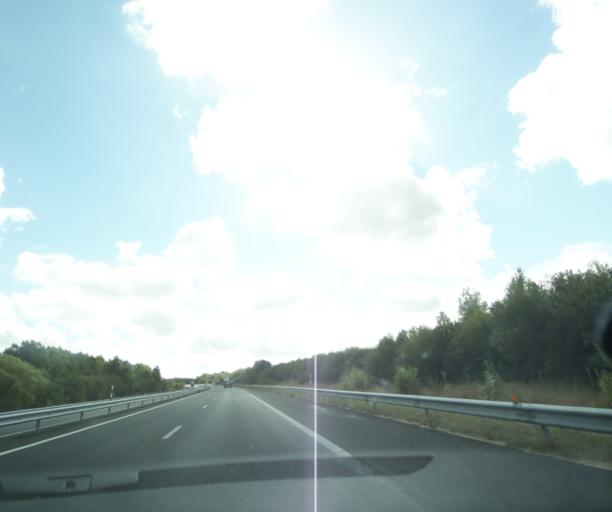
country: FR
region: Poitou-Charentes
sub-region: Departement de la Charente-Maritime
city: Bords
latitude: 45.9145
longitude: -0.8143
